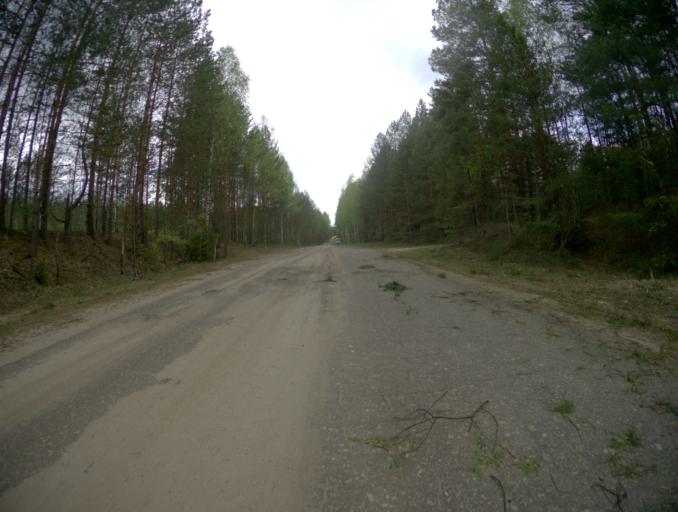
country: RU
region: Vladimir
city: Velikodvorskiy
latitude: 55.2449
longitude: 40.7123
